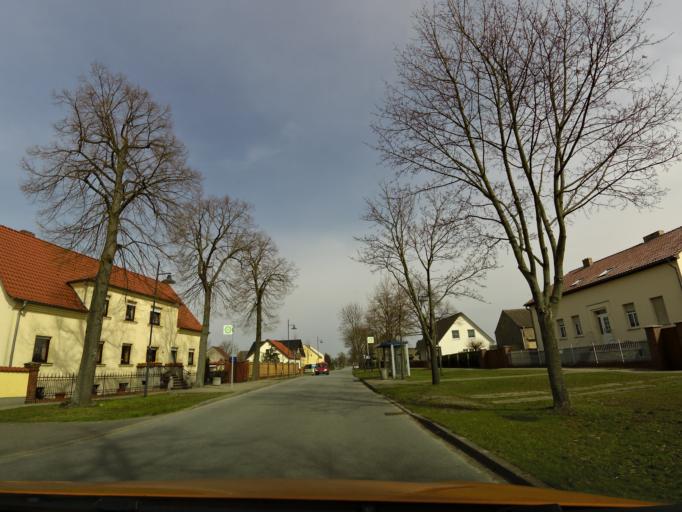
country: DE
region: Brandenburg
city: Stahnsdorf
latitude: 52.3287
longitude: 13.1667
